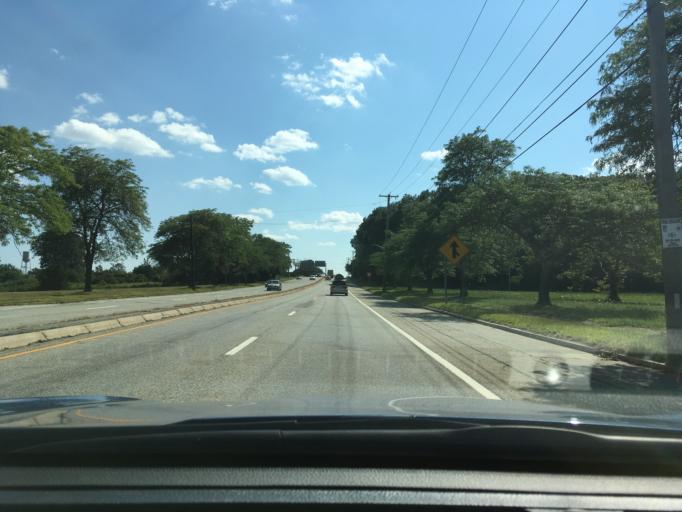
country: US
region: Rhode Island
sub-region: Providence County
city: Cranston
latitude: 41.7524
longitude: -71.4649
